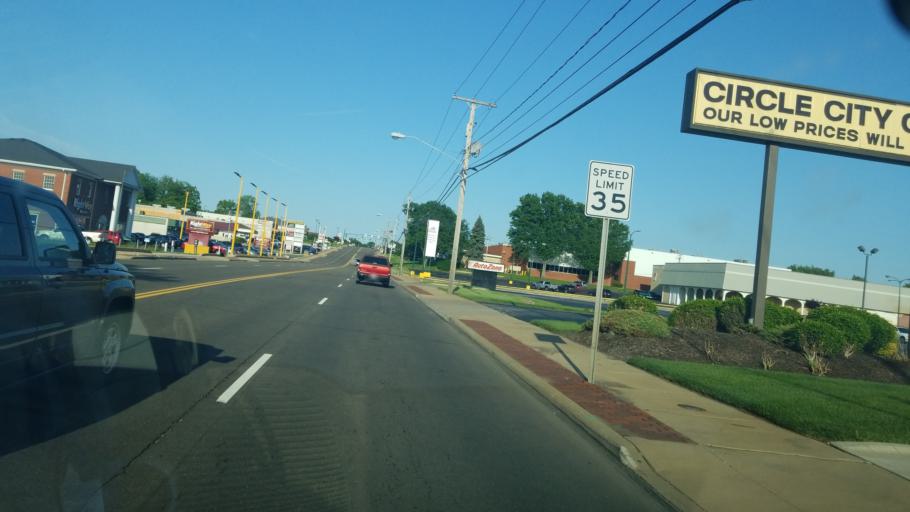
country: US
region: Ohio
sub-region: Summit County
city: Tallmadge
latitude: 41.1016
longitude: -81.4552
